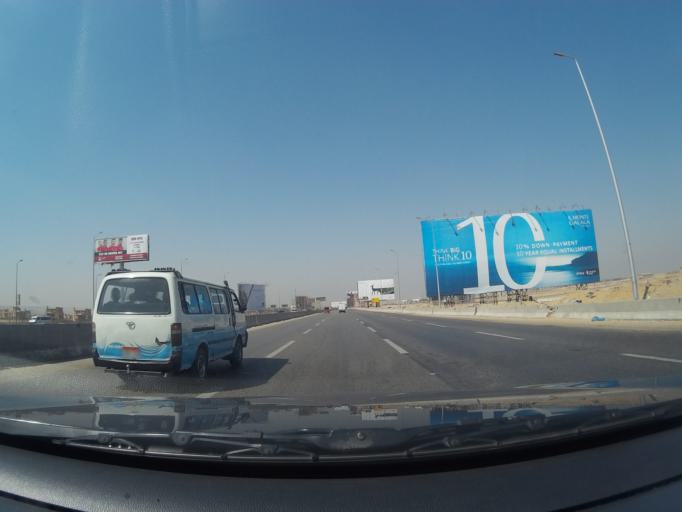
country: EG
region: Muhafazat al Qahirah
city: Cairo
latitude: 29.9955
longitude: 31.3891
